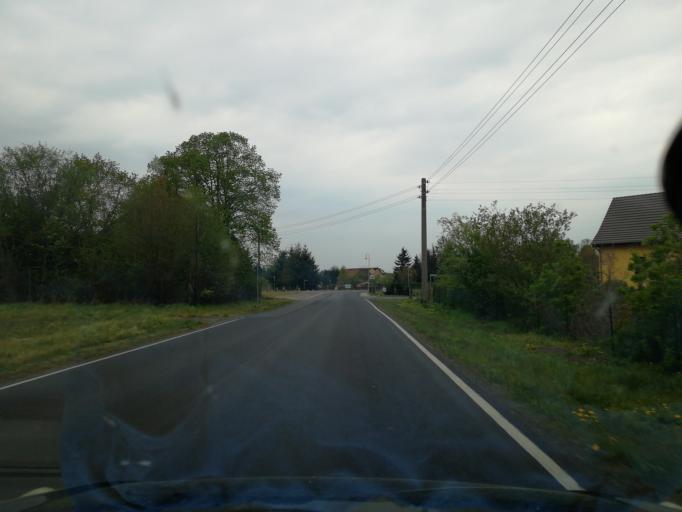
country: DE
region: Brandenburg
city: Calau
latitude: 51.7594
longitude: 13.9152
